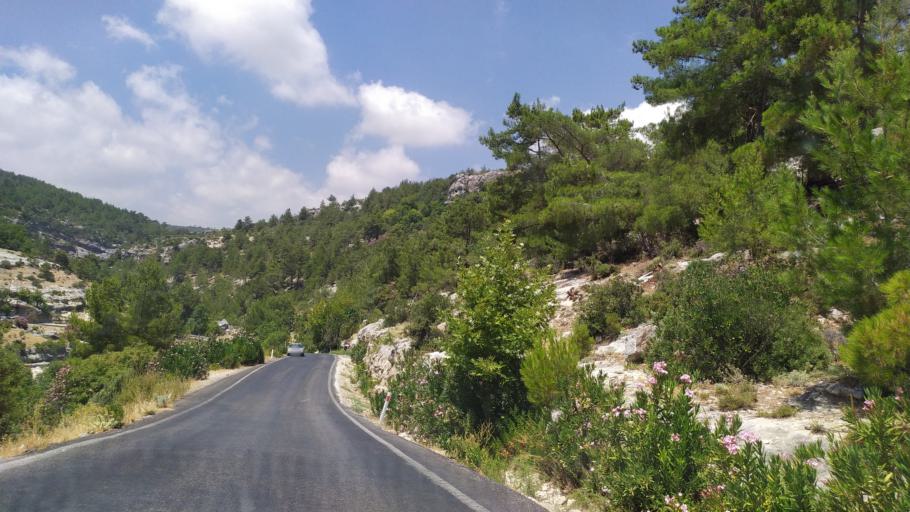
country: TR
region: Mersin
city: Gulnar
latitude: 36.2769
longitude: 33.3821
